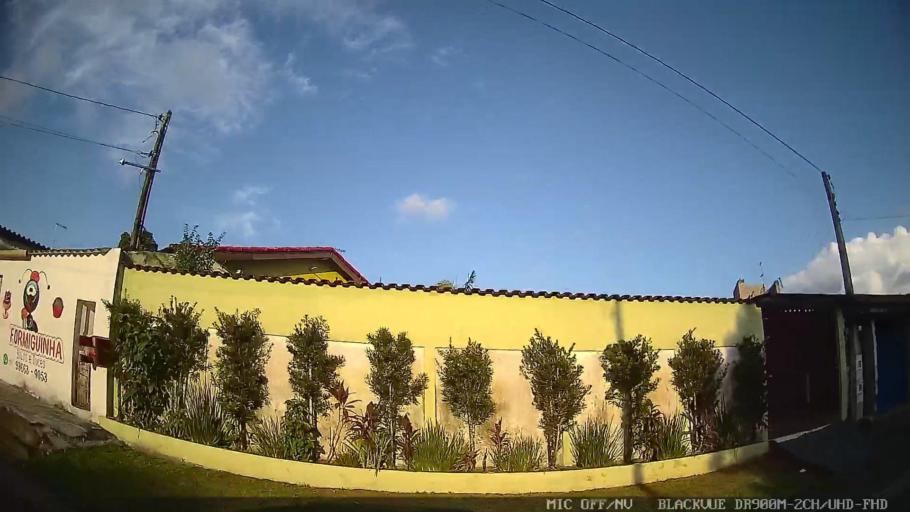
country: BR
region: Sao Paulo
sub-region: Itanhaem
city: Itanhaem
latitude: -24.1810
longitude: -46.8216
